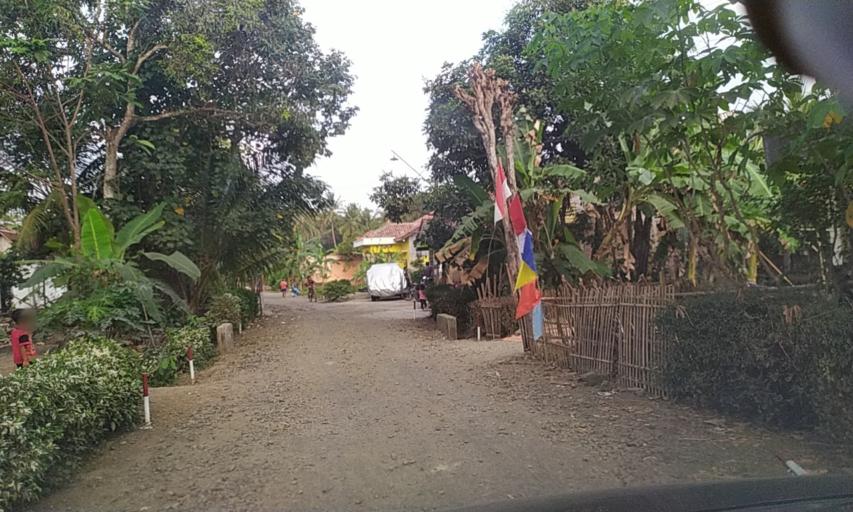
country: ID
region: Central Java
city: Madusari
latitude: -7.6188
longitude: 109.0879
